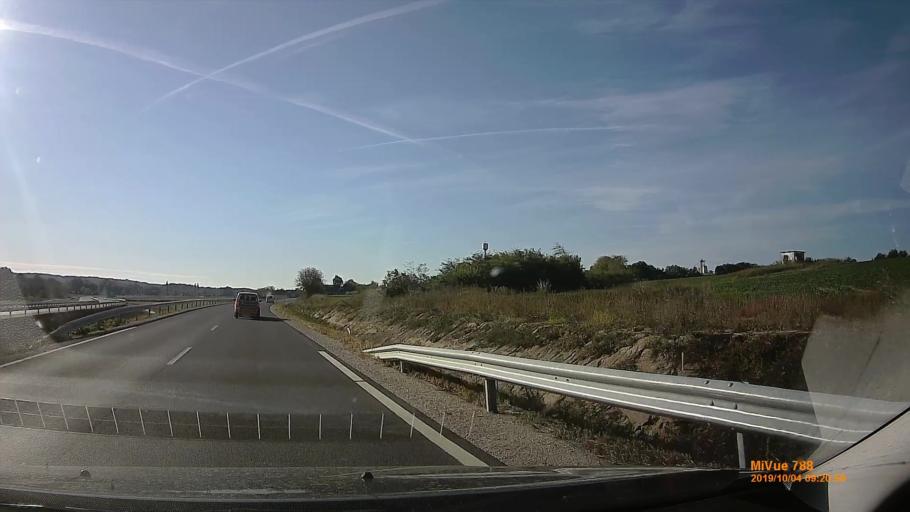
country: HU
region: Somogy
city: Karad
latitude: 46.5596
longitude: 17.8100
